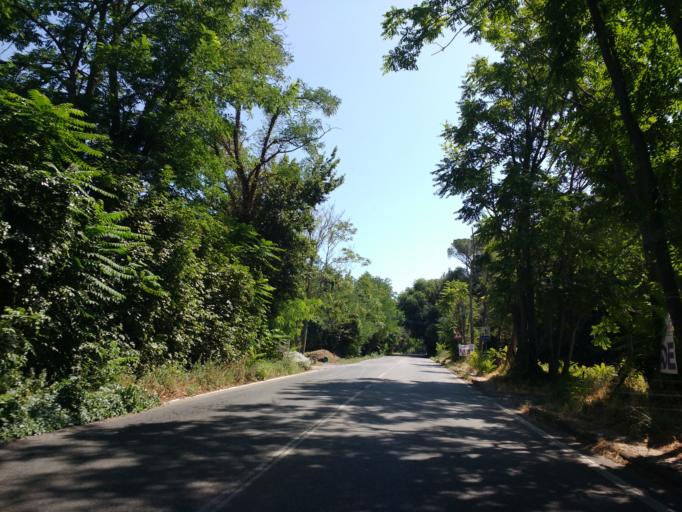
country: IT
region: Latium
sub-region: Citta metropolitana di Roma Capitale
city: Grottaferrata
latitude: 41.7970
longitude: 12.6827
